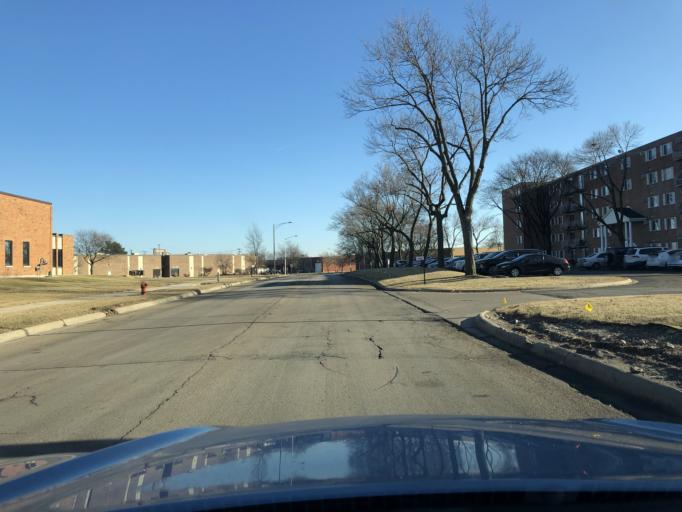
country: US
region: Illinois
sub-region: DuPage County
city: Roselle
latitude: 41.9866
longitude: -88.0429
